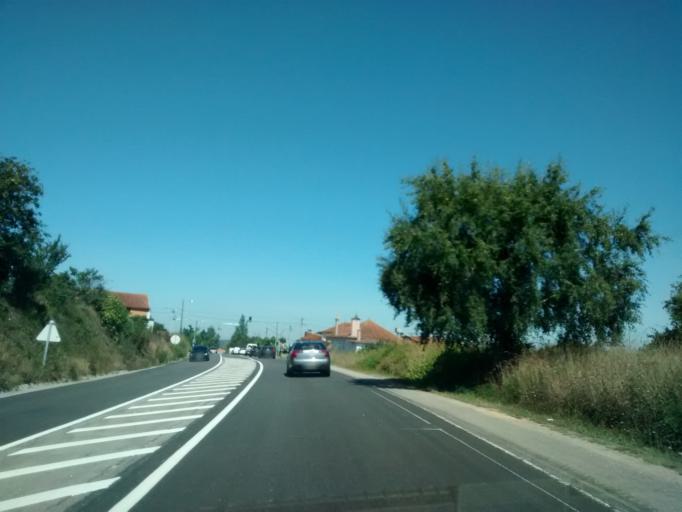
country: PT
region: Aveiro
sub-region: Oliveira do Bairro
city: Oia
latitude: 40.5468
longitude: -8.5365
